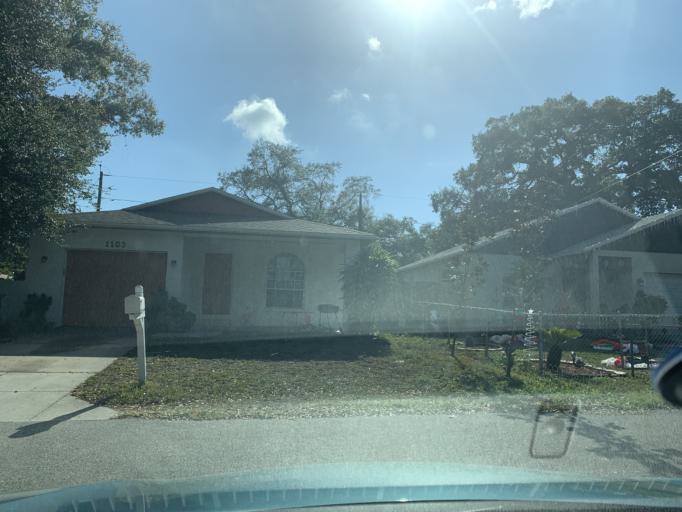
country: US
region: Florida
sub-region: Pinellas County
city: Belleair
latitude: 27.9315
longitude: -82.7993
